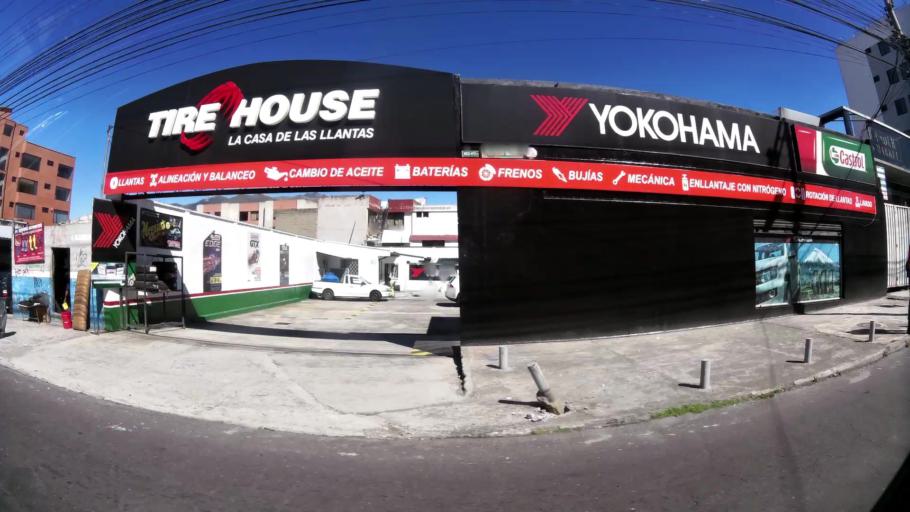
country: EC
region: Pichincha
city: Quito
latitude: -0.1386
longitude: -78.4701
